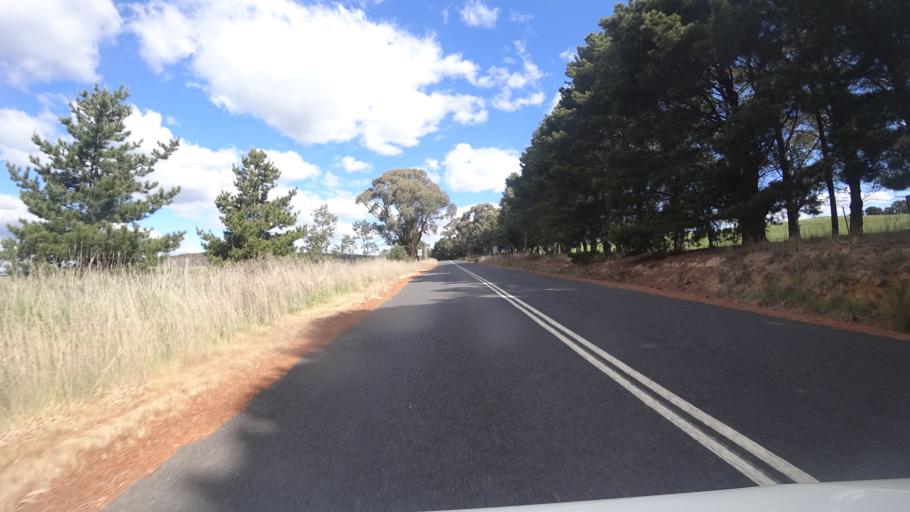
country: AU
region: New South Wales
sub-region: Oberon
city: Oberon
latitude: -33.6749
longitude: 149.7849
